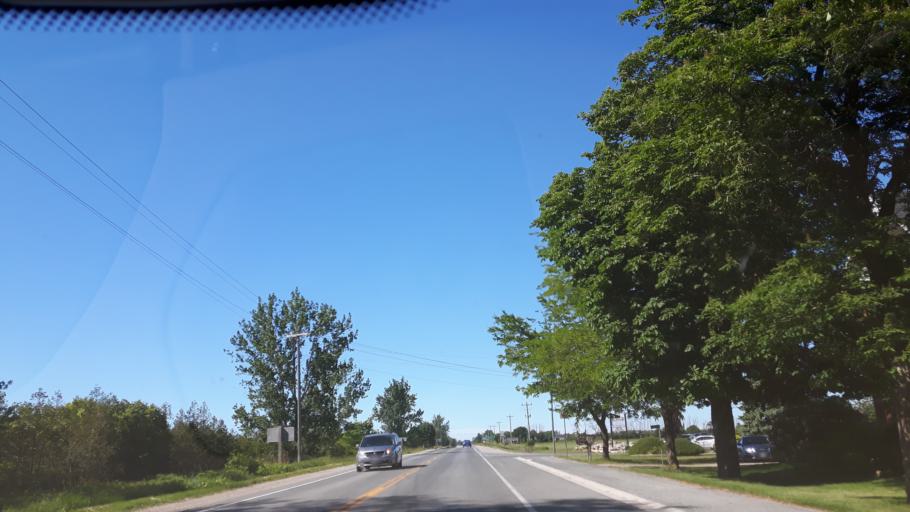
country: CA
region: Ontario
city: Bluewater
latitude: 43.4147
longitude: -81.7058
